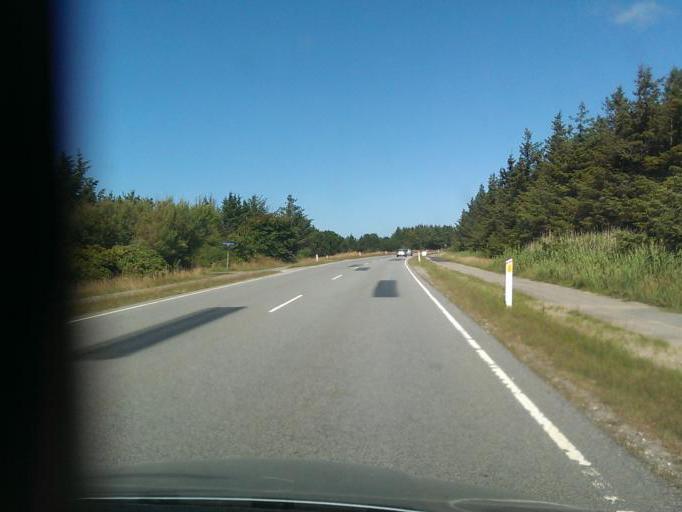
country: DK
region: North Denmark
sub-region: Jammerbugt Kommune
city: Pandrup
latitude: 57.3571
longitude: 9.7077
